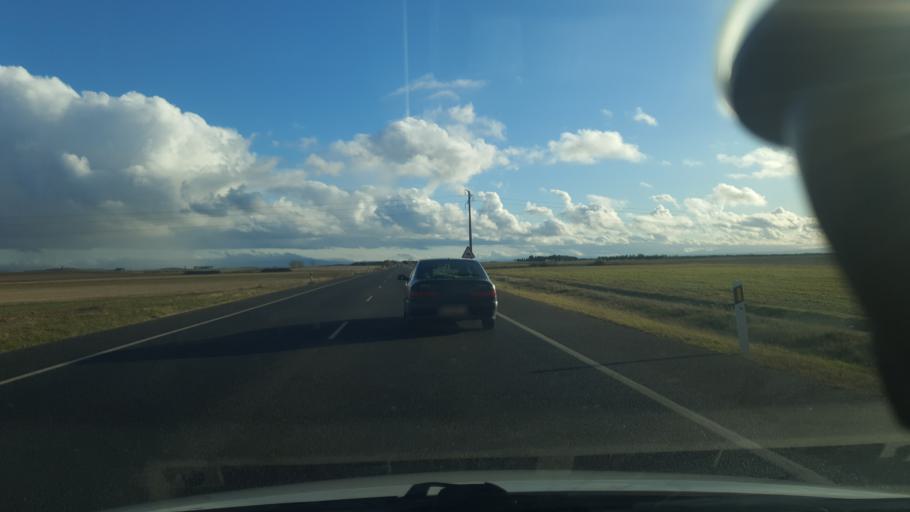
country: ES
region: Castille and Leon
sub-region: Provincia de Segovia
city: Rapariegos
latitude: 41.0867
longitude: -4.6367
